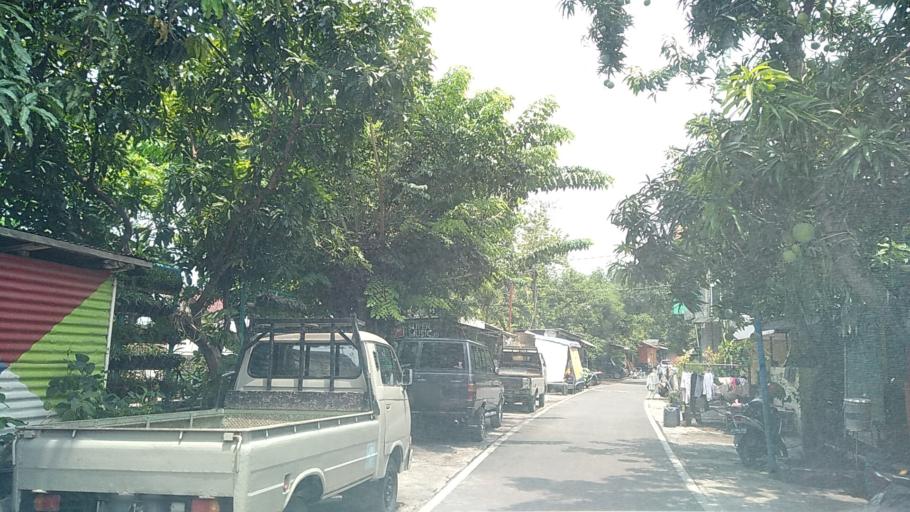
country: ID
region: Central Java
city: Semarang
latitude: -6.9863
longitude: 110.3917
